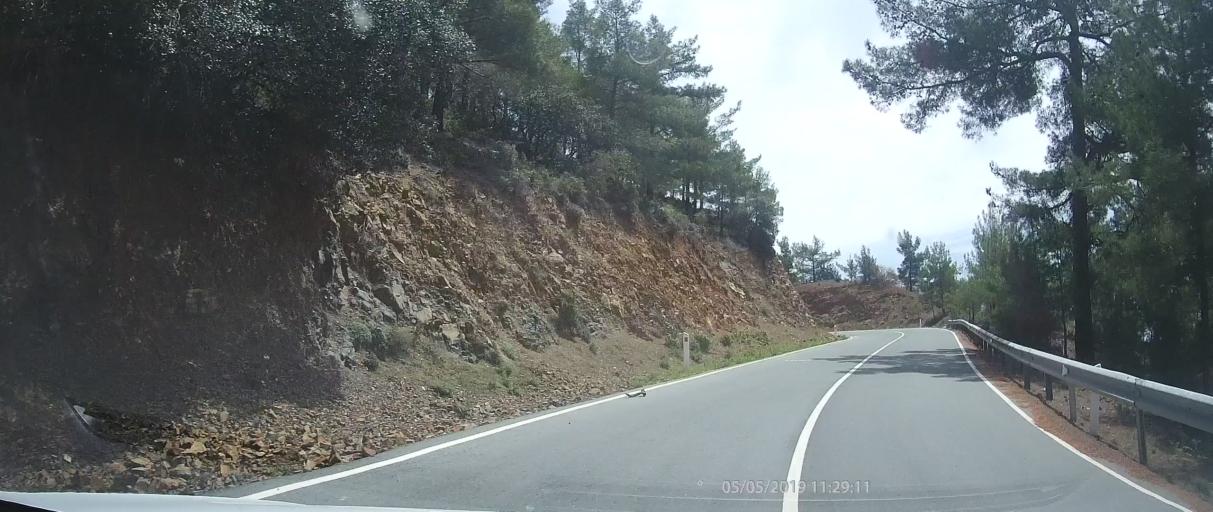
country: CY
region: Limassol
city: Pachna
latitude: 34.9407
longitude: 32.6485
